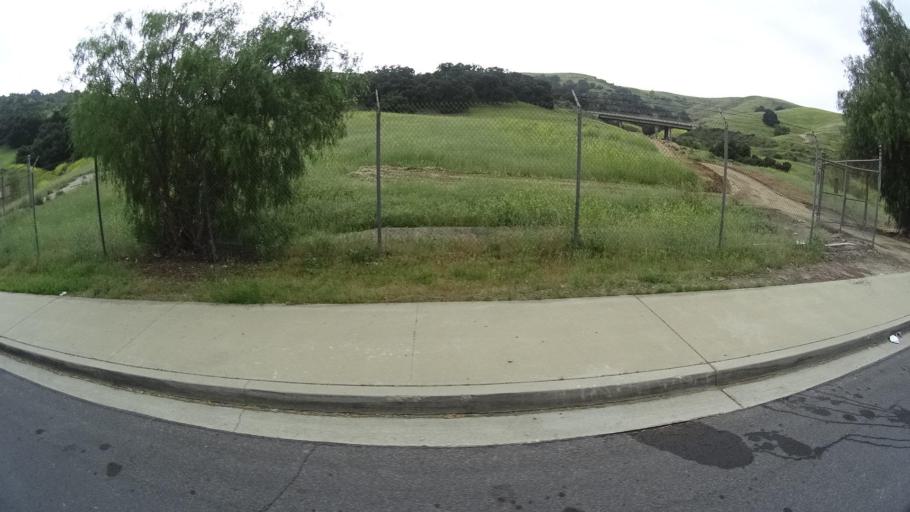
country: US
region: California
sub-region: San Bernardino County
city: Chino Hills
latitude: 34.0204
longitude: -117.7695
